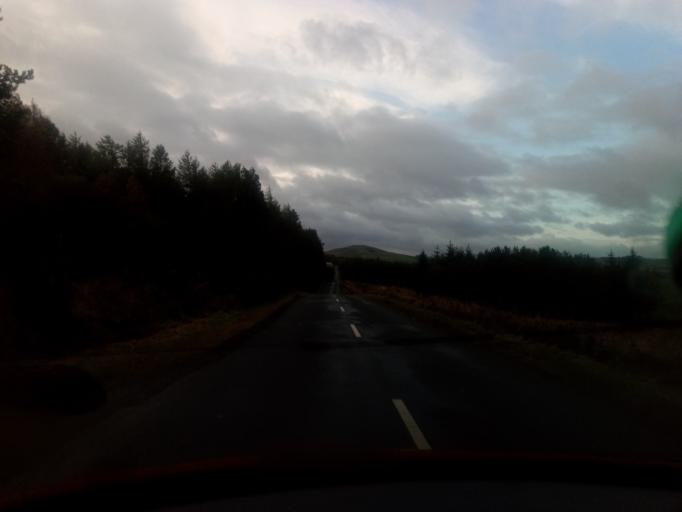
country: GB
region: Scotland
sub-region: The Scottish Borders
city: Jedburgh
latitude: 55.4308
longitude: -2.6100
